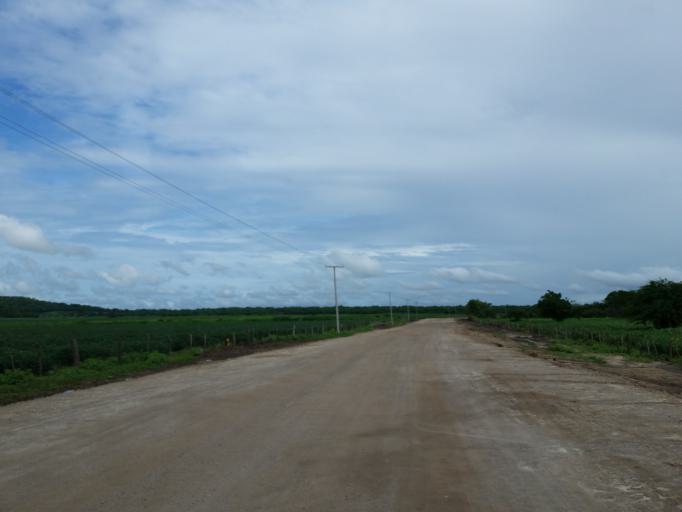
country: NI
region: Leon
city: Larreynaga
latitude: 12.5494
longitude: -86.6197
